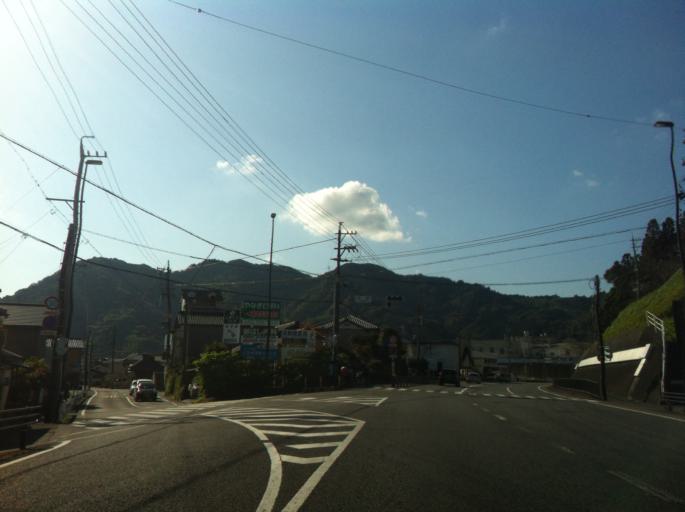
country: JP
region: Shizuoka
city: Shizuoka-shi
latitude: 34.9484
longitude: 138.3581
